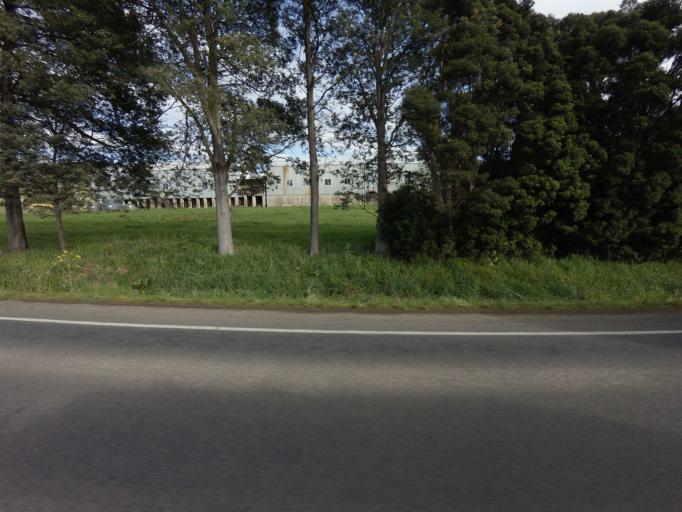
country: AU
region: Tasmania
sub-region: Huon Valley
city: Huonville
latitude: -43.0442
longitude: 147.0434
